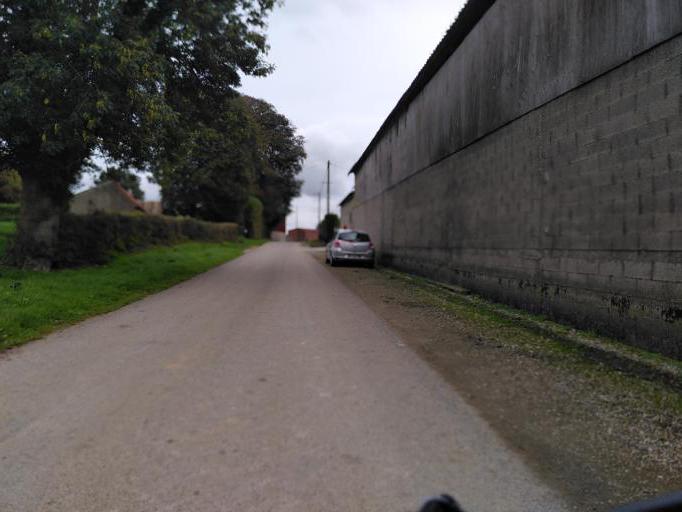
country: FR
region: Nord-Pas-de-Calais
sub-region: Departement du Pas-de-Calais
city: Desvres
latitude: 50.6504
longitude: 1.9327
